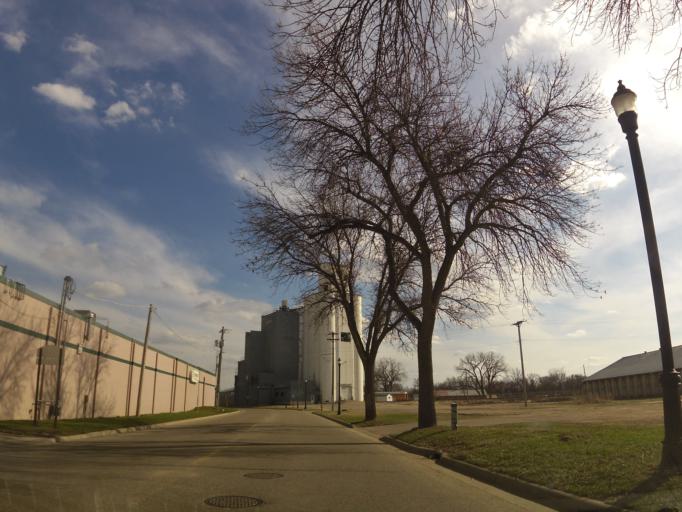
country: US
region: Minnesota
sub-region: Chippewa County
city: Montevideo
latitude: 44.9442
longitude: -95.7262
